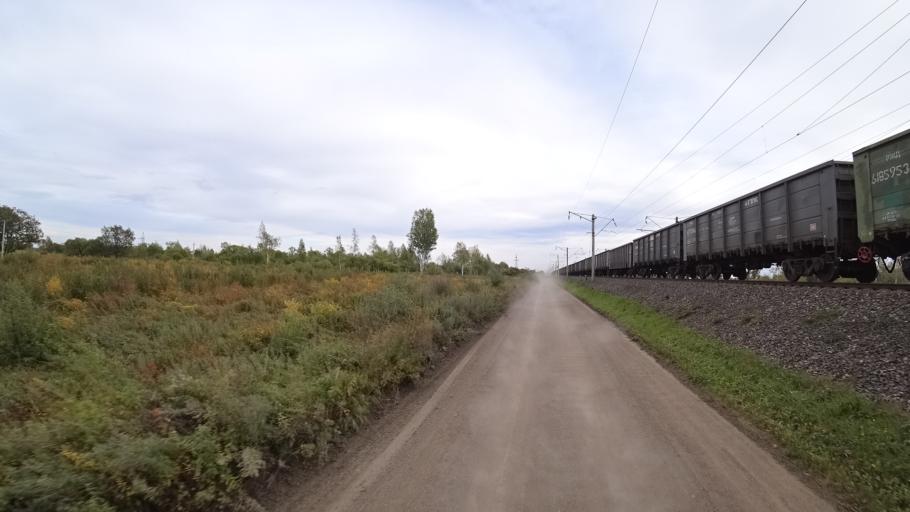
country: RU
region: Amur
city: Arkhara
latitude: 49.3679
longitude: 130.1431
